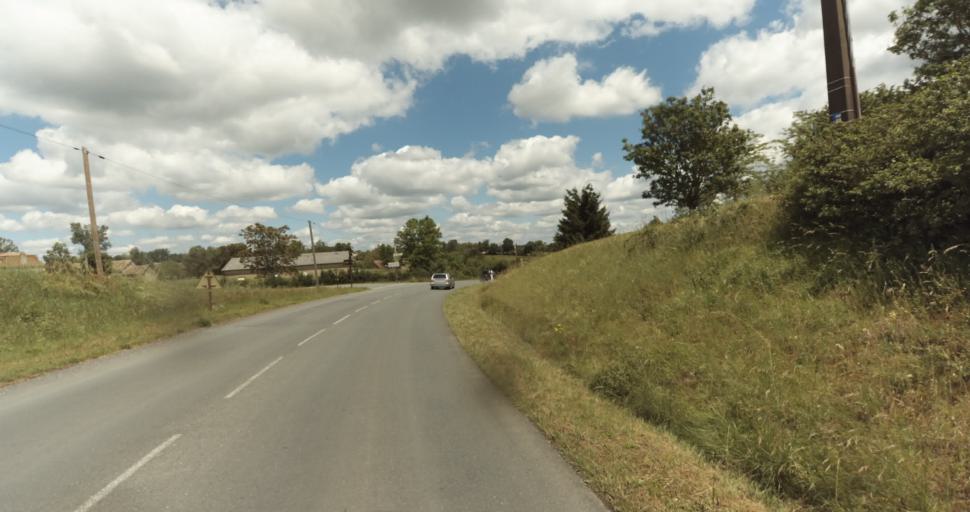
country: FR
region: Aquitaine
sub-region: Departement de la Dordogne
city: Beaumont-du-Perigord
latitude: 44.7391
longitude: 0.7516
